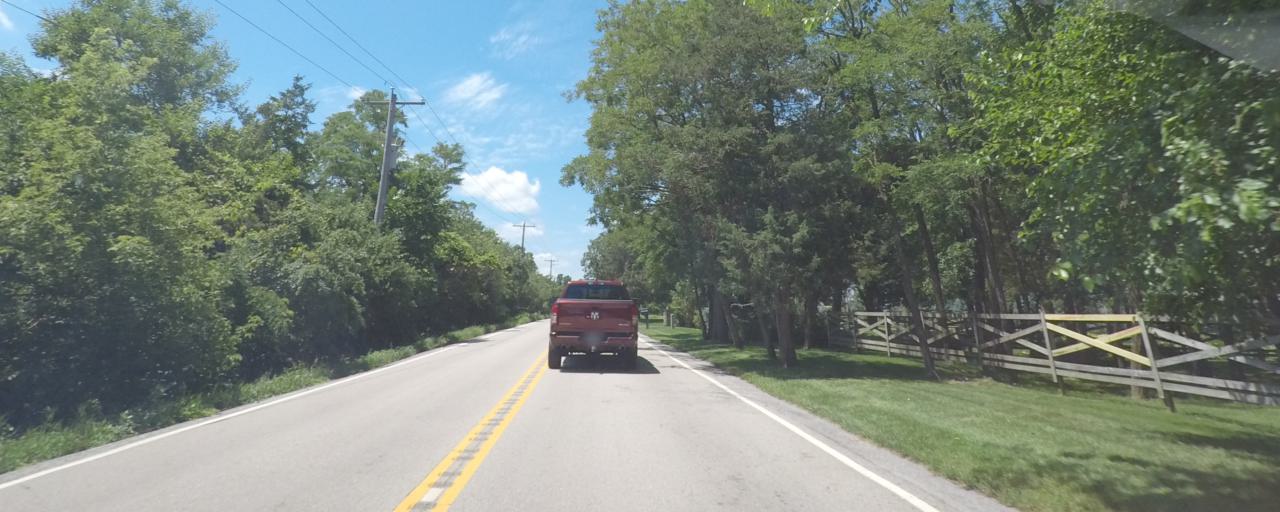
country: US
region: Wisconsin
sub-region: Jefferson County
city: Palmyra
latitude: 42.9277
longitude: -88.5330
